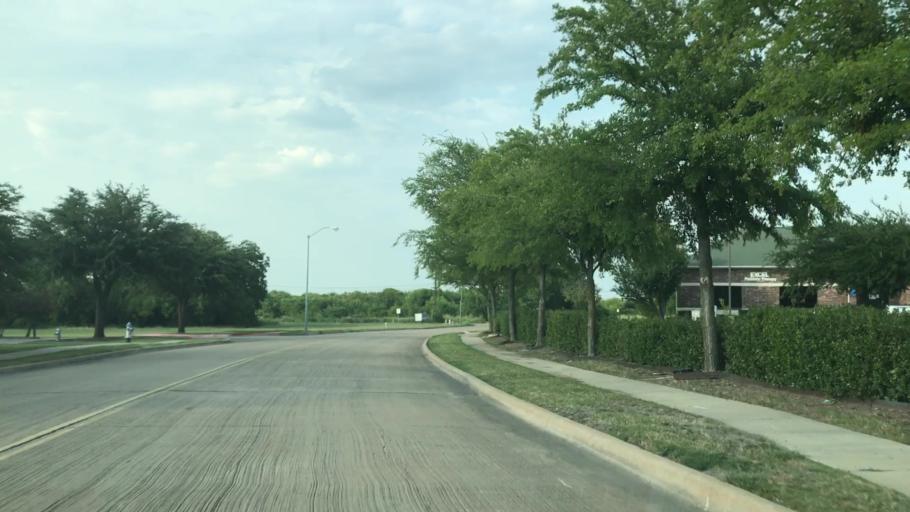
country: US
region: Texas
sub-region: Rockwall County
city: Rockwall
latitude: 32.9179
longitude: -96.4536
